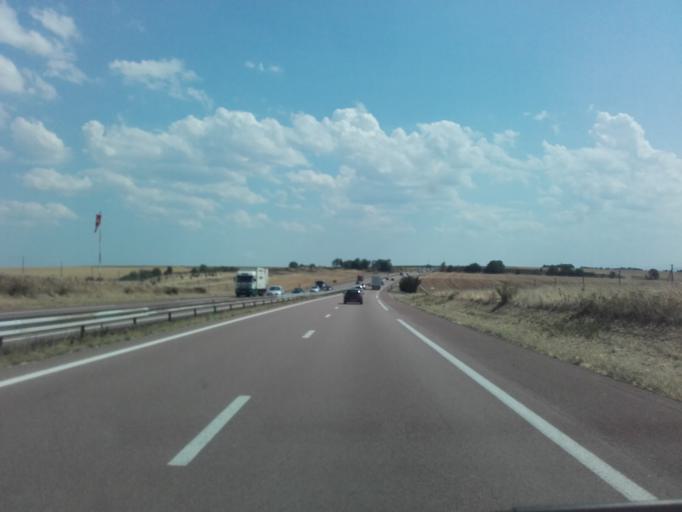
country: FR
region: Bourgogne
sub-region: Departement de l'Yonne
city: Joux-la-Ville
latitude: 47.5767
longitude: 3.9341
